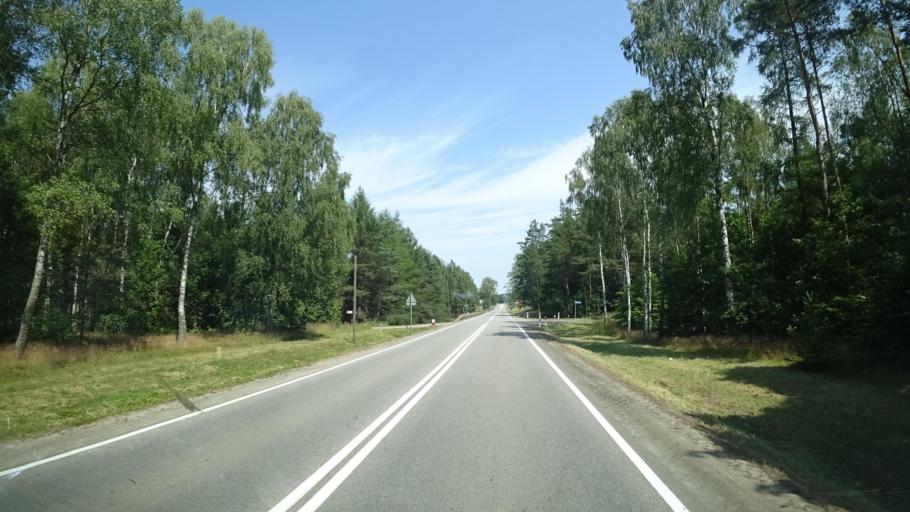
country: PL
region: Pomeranian Voivodeship
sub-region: Powiat koscierski
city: Grabowo Koscierskie
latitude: 54.1824
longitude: 18.0936
